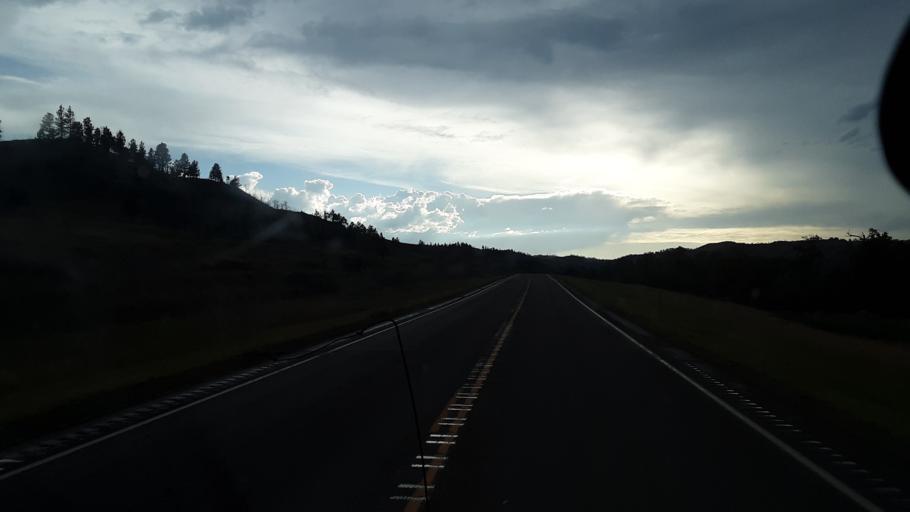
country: US
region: Montana
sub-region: Rosebud County
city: Lame Deer
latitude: 45.6185
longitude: -106.3996
